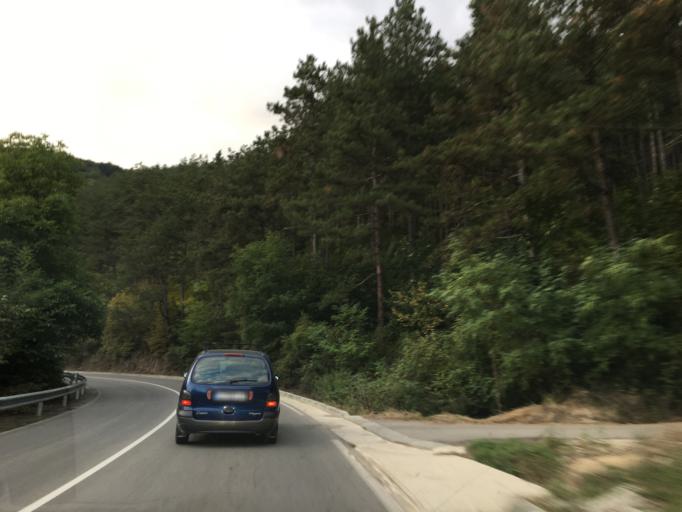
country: BG
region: Sofiya
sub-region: Obshtina Svoge
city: Svoge
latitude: 42.8822
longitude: 23.3794
